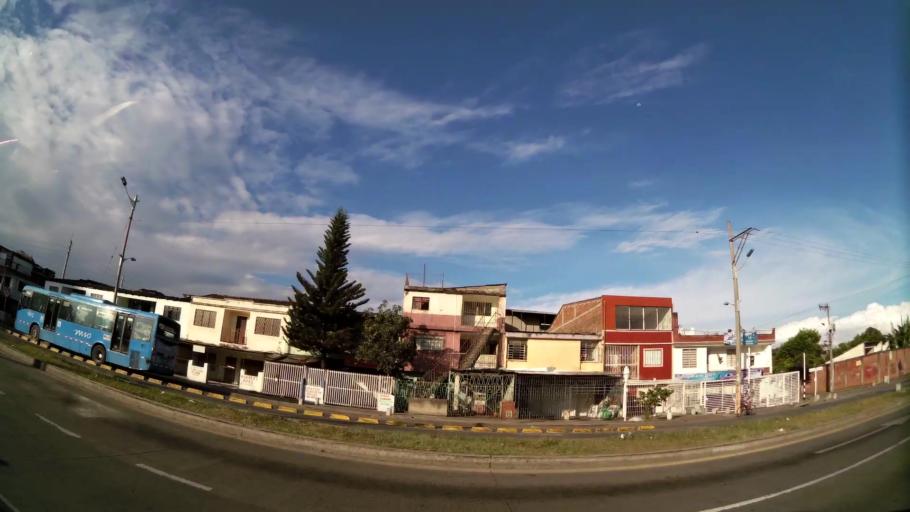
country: CO
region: Valle del Cauca
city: Cali
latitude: 3.4352
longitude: -76.5146
